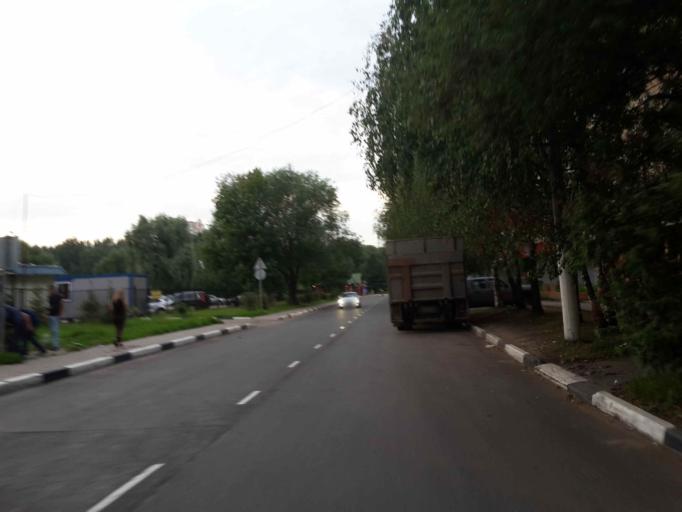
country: RU
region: Moskovskaya
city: Dolgoprudnyy
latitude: 55.9415
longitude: 37.5034
